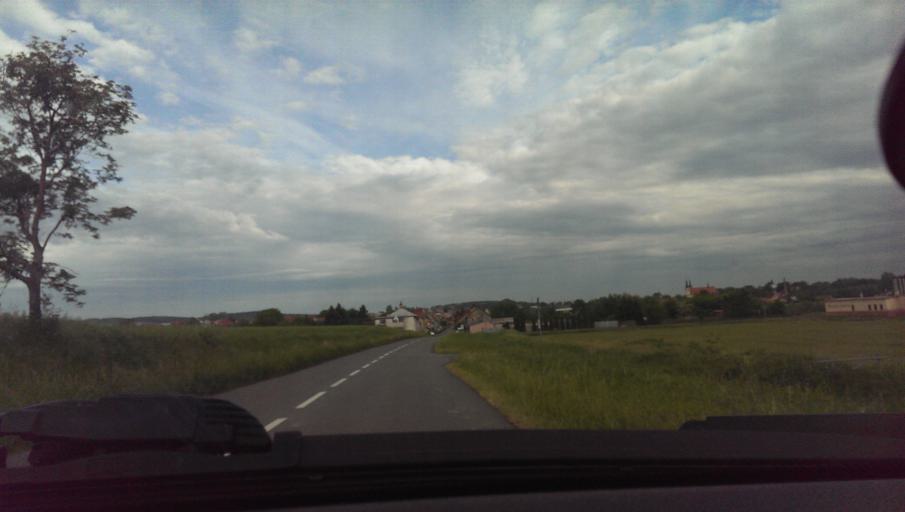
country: CZ
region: Zlin
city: Kvasice
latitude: 49.2347
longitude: 17.4803
